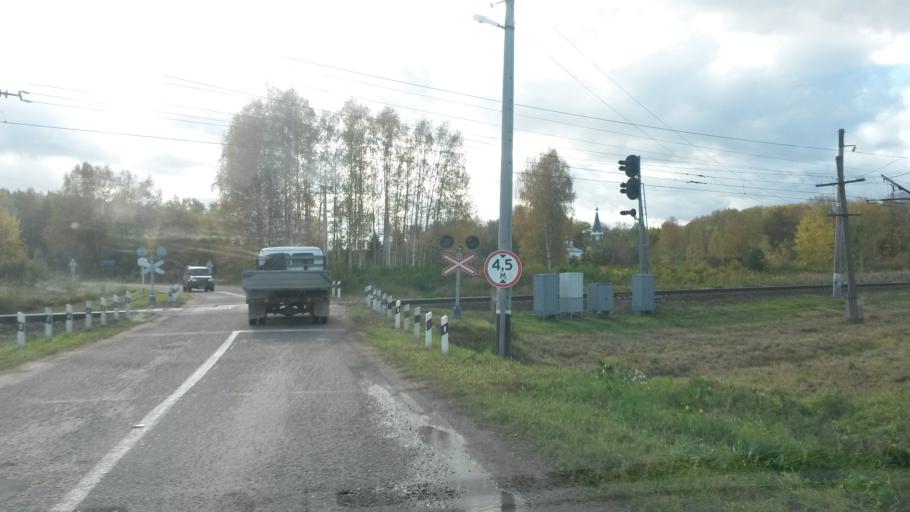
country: RU
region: Jaroslavl
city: Yaroslavl
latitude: 57.5254
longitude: 39.9752
